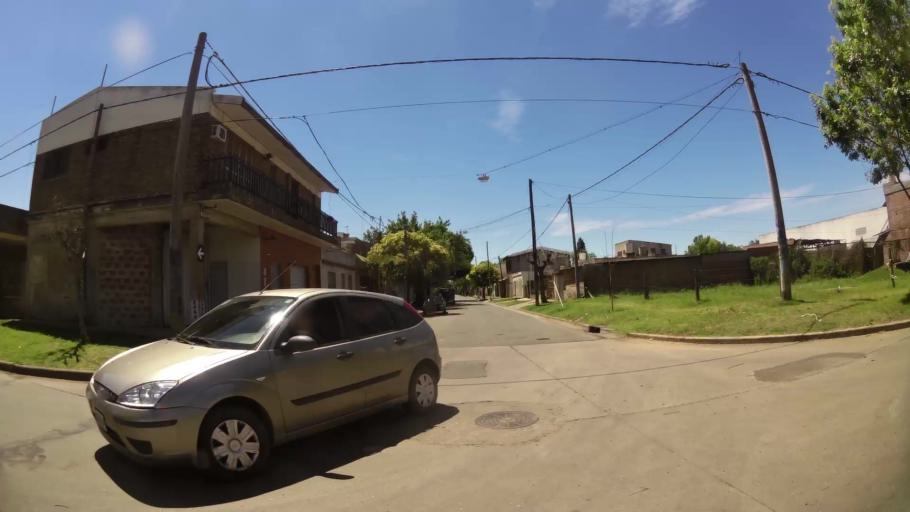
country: AR
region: Santa Fe
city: Perez
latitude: -32.9448
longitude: -60.7216
